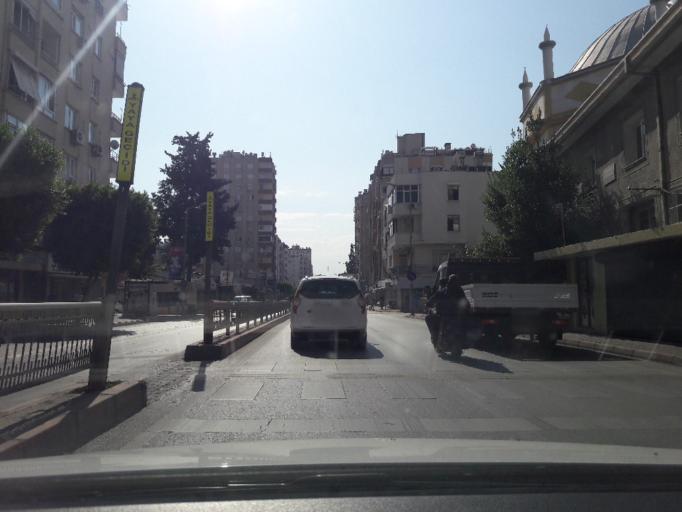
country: TR
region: Adana
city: Adana
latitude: 37.0119
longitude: 35.3230
